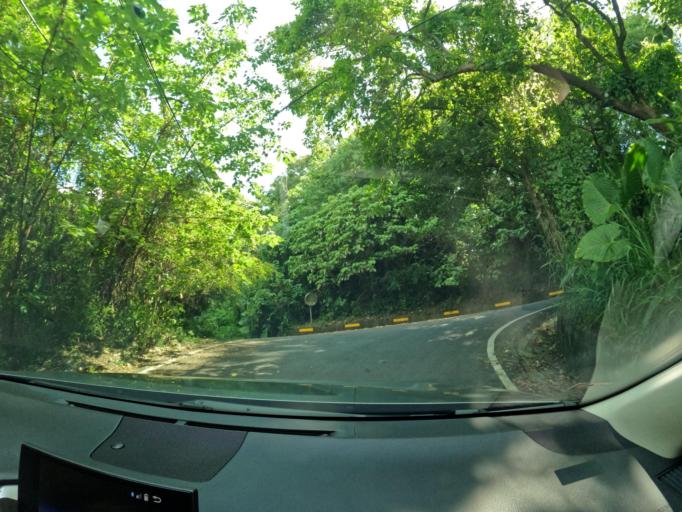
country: TW
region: Taiwan
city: Fengyuan
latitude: 24.3115
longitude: 120.7670
